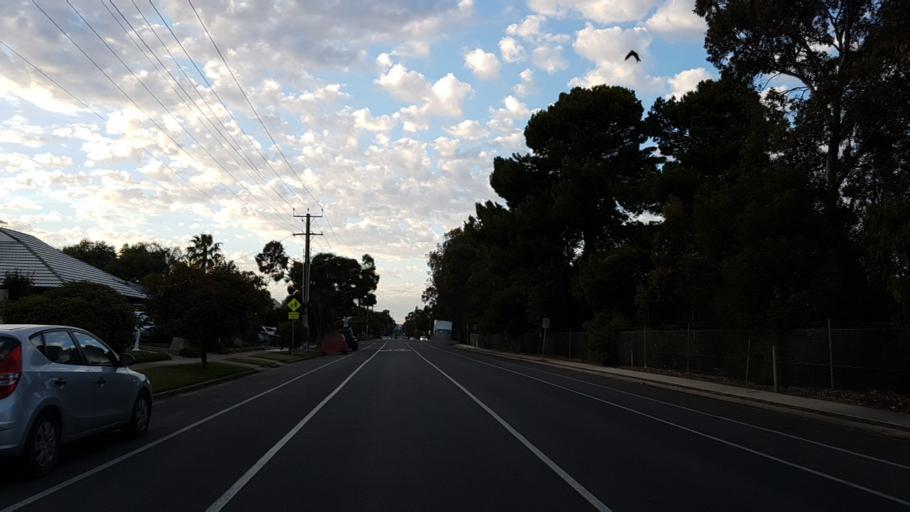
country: AU
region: South Australia
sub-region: City of West Torrens
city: Plympton
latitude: -34.9290
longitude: 138.5343
